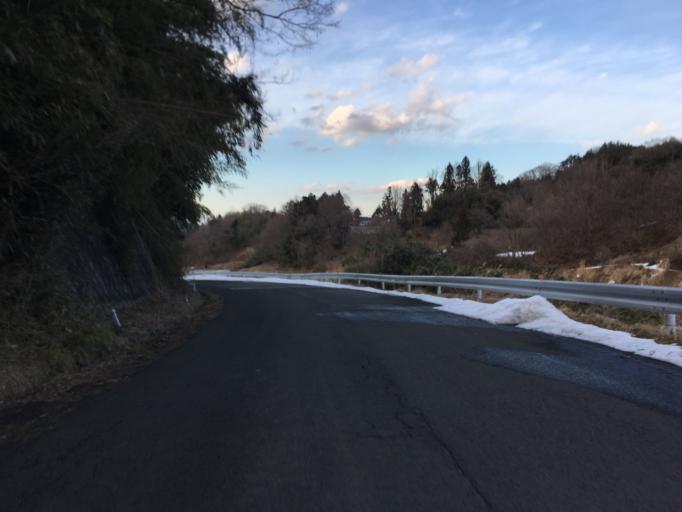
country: JP
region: Fukushima
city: Fukushima-shi
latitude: 37.6414
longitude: 140.5898
